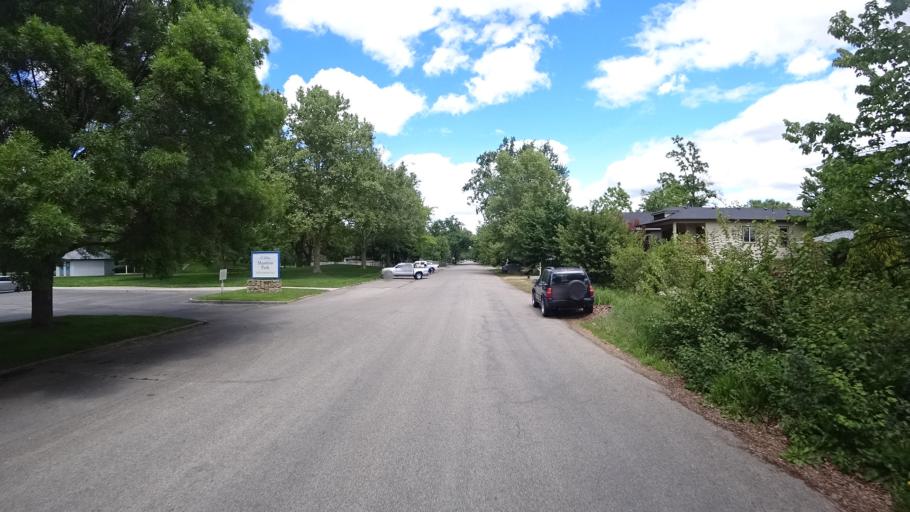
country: US
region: Idaho
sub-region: Ada County
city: Boise
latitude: 43.5870
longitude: -116.1986
